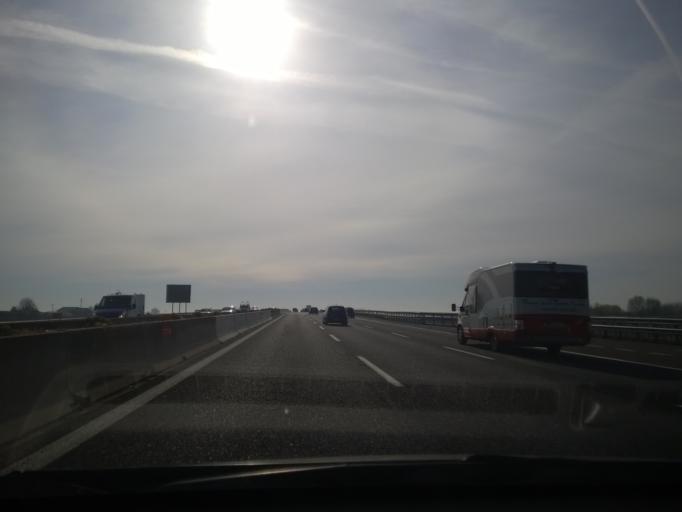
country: IT
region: Emilia-Romagna
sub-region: Provincia di Ravenna
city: Solarolo
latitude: 44.3515
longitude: 11.8235
